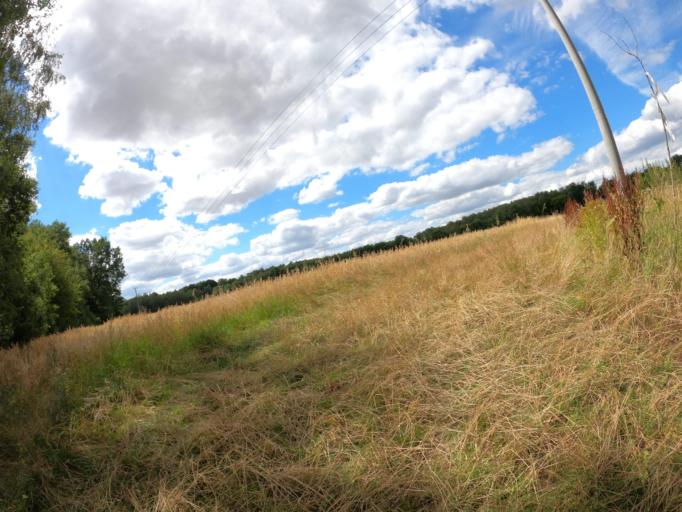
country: PL
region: West Pomeranian Voivodeship
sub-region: Powiat swidwinski
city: Swidwin
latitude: 53.7485
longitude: 15.8243
